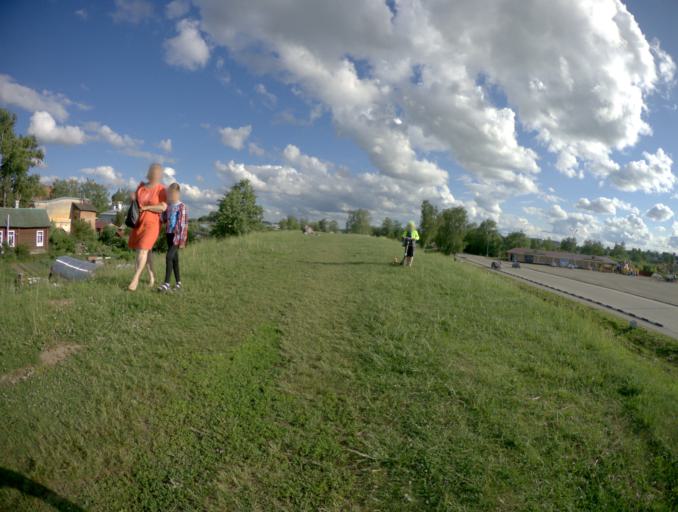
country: RU
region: Vladimir
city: Yur'yev-Pol'skiy
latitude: 56.4978
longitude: 39.6783
